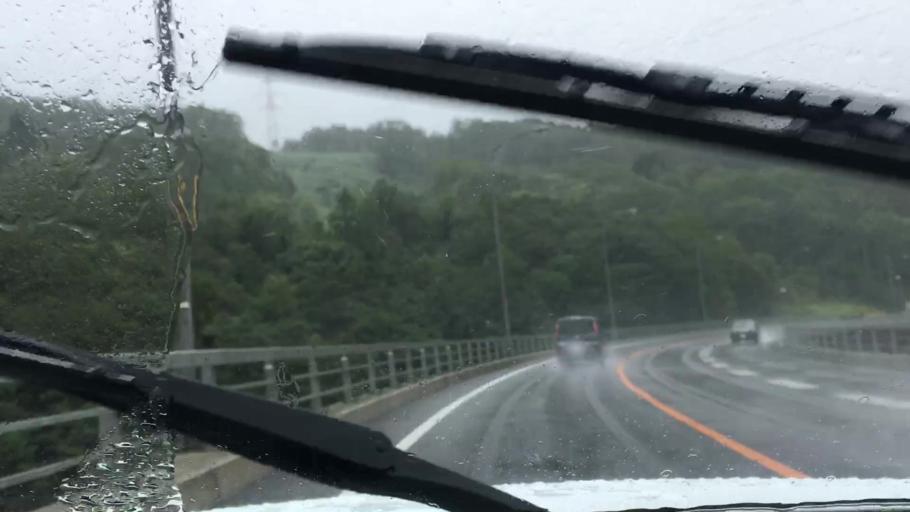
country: JP
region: Hokkaido
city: Sapporo
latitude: 42.8513
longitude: 141.0917
